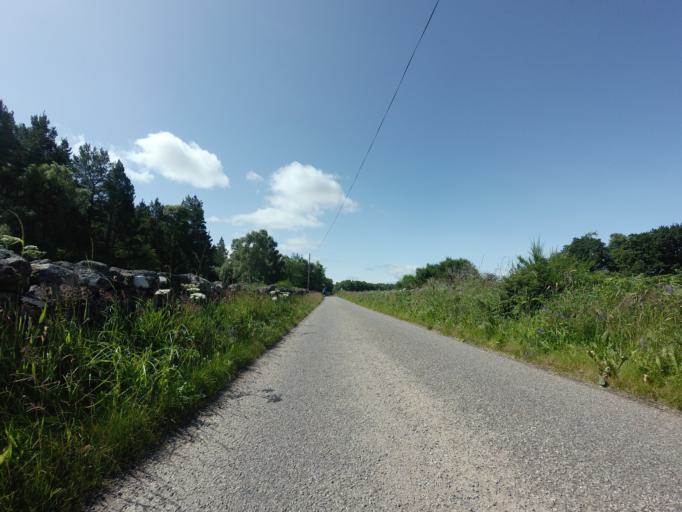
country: GB
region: Scotland
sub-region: Highland
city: Nairn
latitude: 57.5004
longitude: -3.9401
